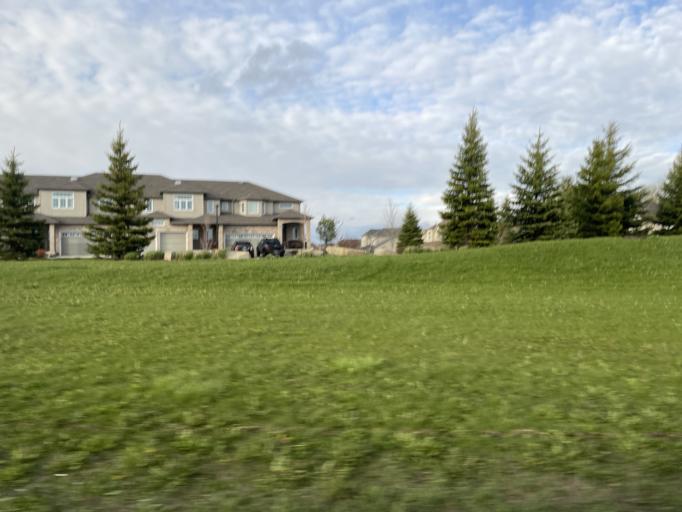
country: CA
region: Ontario
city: Waterloo
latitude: 43.4844
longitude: -80.4127
